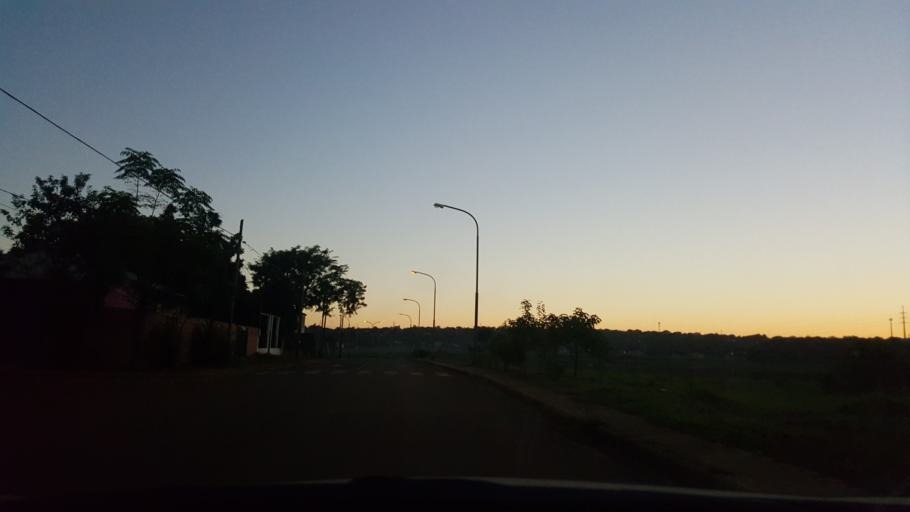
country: AR
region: Misiones
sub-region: Departamento de Capital
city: Posadas
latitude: -27.4213
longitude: -55.9033
